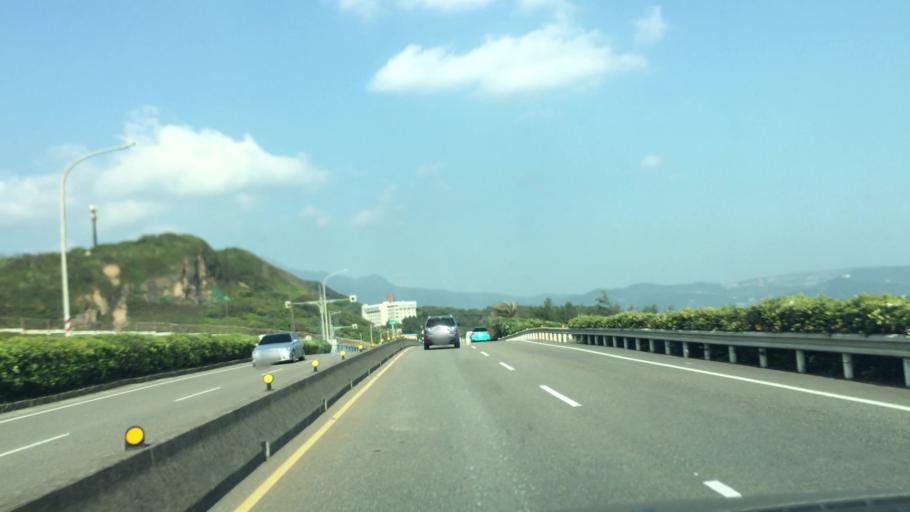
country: TW
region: Taiwan
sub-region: Keelung
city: Keelung
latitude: 25.2057
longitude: 121.6643
